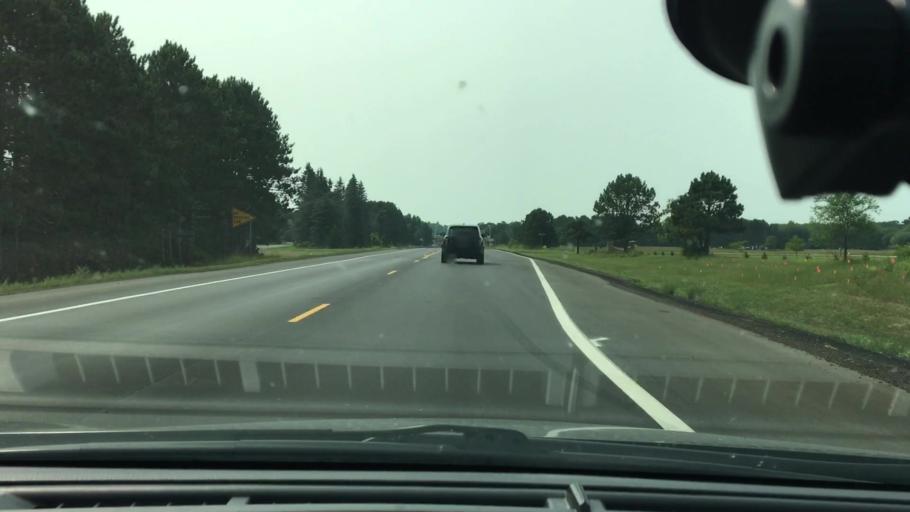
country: US
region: Minnesota
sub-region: Crow Wing County
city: Brainerd
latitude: 46.4033
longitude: -94.1762
